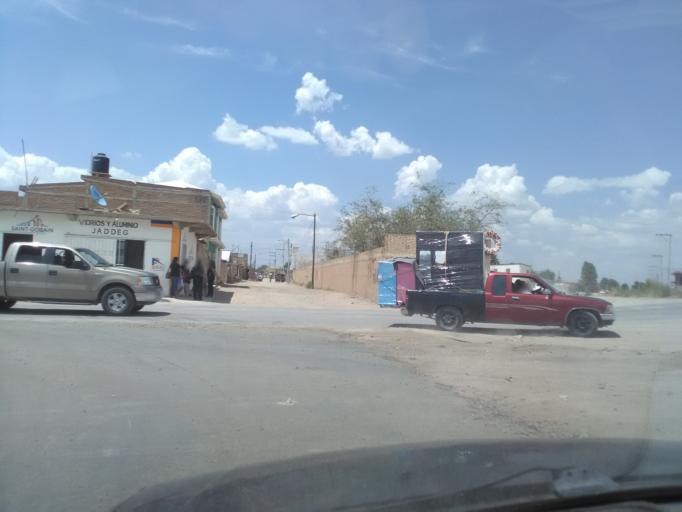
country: MX
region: Durango
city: Victoria de Durango
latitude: 24.0119
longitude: -104.6097
